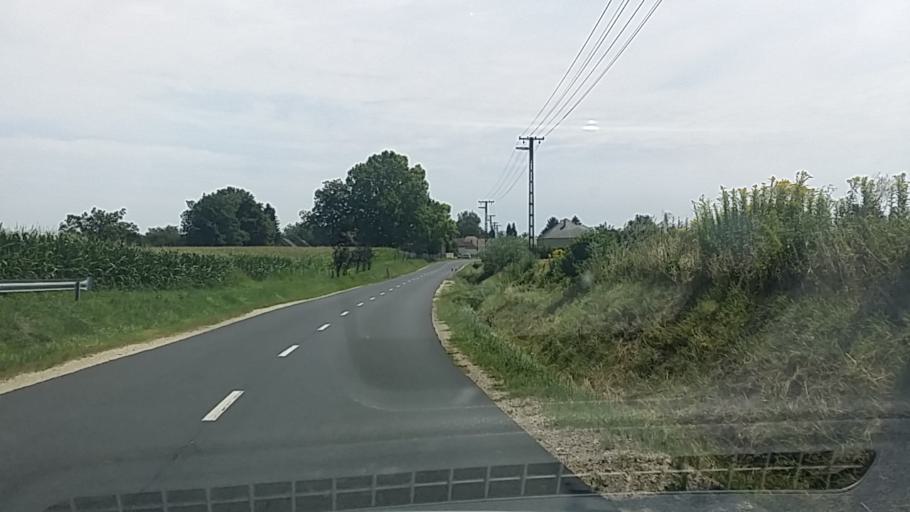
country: HU
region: Zala
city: Letenye
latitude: 46.4233
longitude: 16.7390
